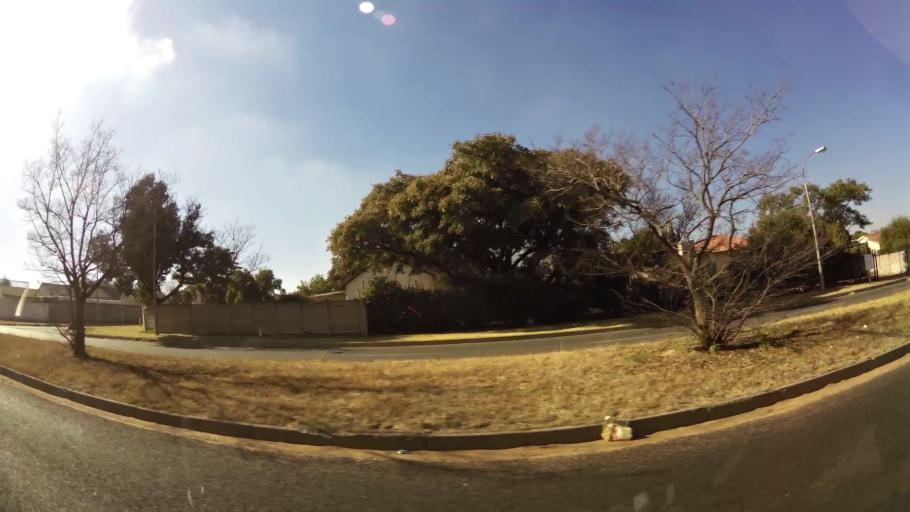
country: ZA
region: Gauteng
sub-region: City of Johannesburg Metropolitan Municipality
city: Roodepoort
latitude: -26.1465
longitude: 27.8243
